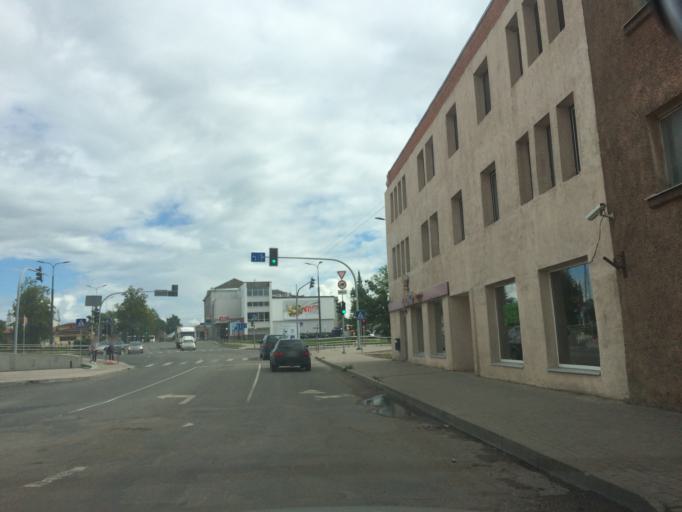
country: LV
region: Rezekne
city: Rezekne
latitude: 56.5005
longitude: 27.3267
